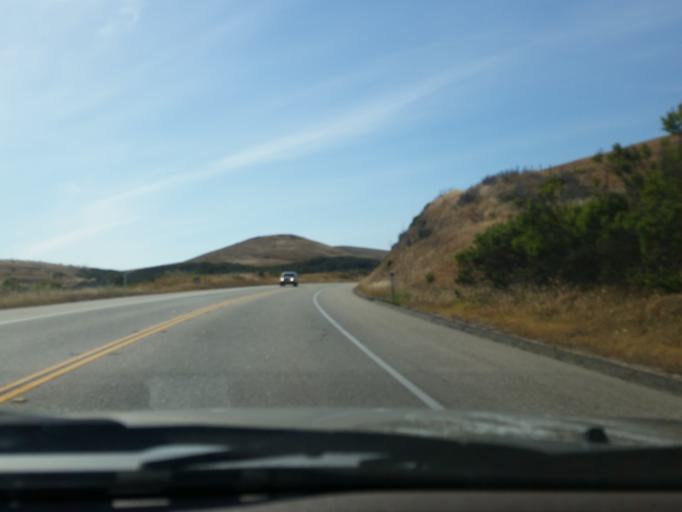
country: US
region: California
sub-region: San Luis Obispo County
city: Cayucos
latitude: 35.4739
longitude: -120.9877
